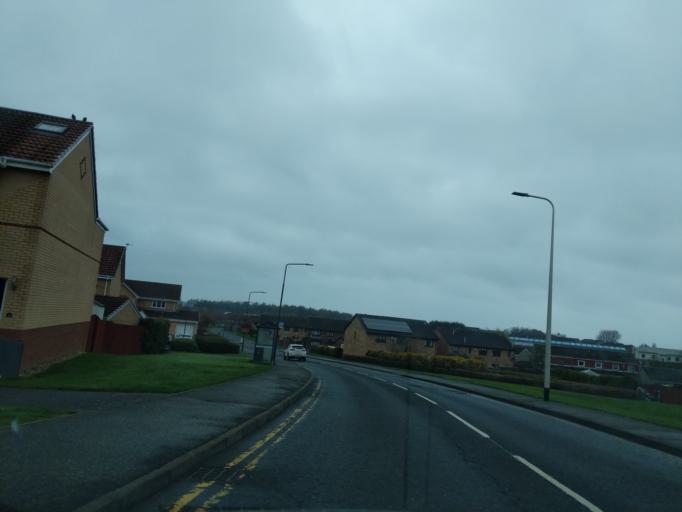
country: GB
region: Scotland
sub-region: East Lothian
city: Musselburgh
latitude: 55.9342
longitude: -3.0710
